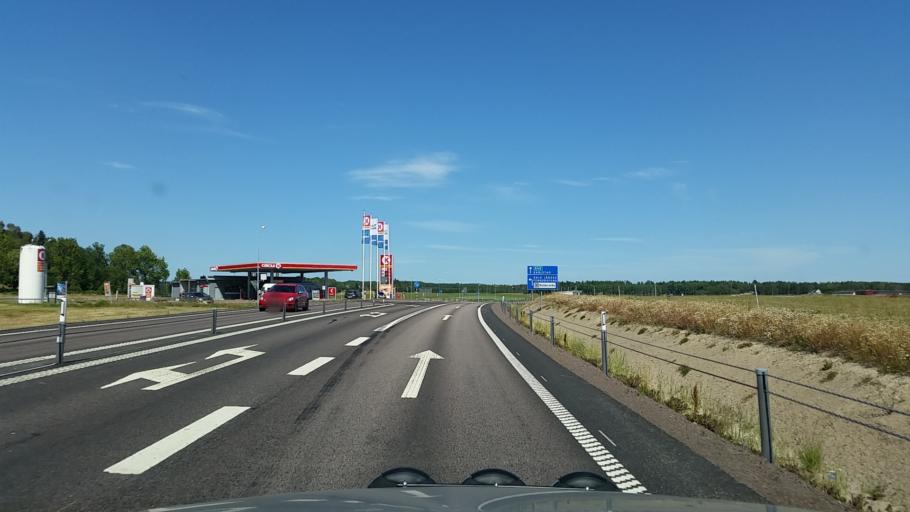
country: SE
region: Vaestra Goetaland
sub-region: Amals Kommun
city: Amal
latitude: 58.9724
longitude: 12.6214
